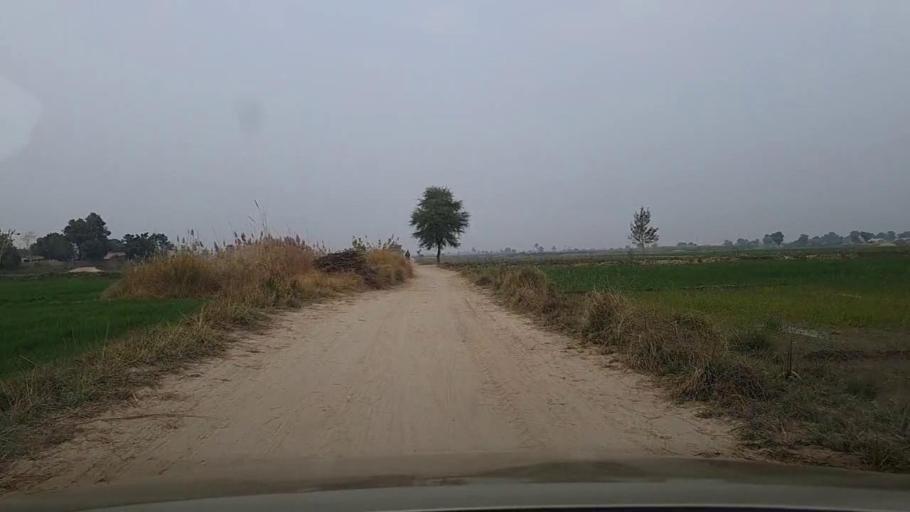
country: PK
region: Sindh
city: Sanghar
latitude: 26.1358
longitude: 68.9265
